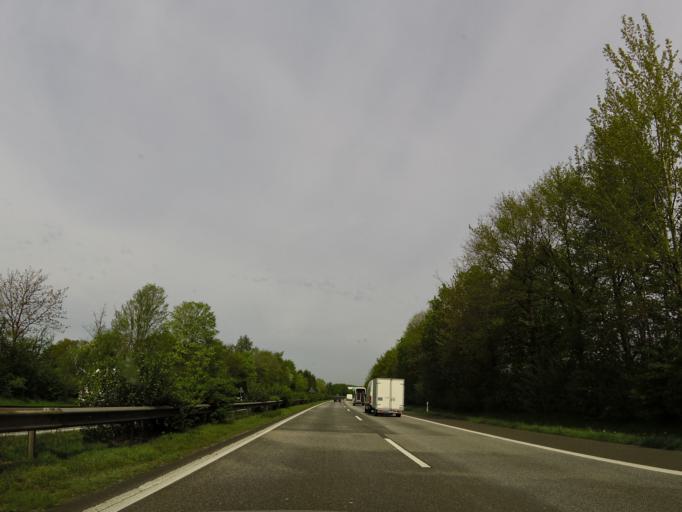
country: DE
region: Schleswig-Holstein
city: Seeth-Ekholt
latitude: 53.7326
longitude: 9.7222
